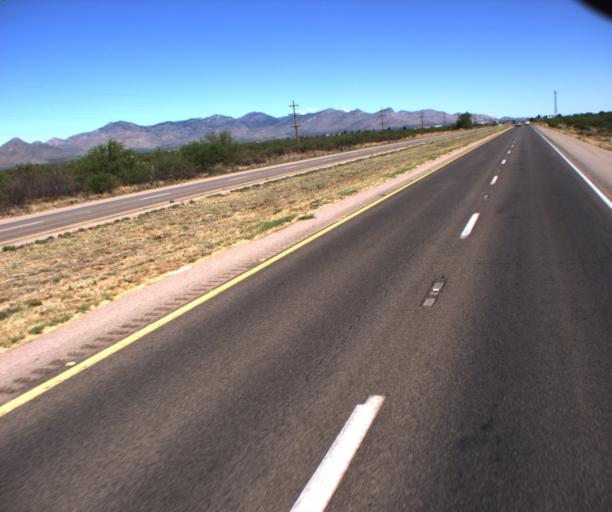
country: US
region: Arizona
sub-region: Cochise County
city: Huachuca City
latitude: 31.6720
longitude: -110.3502
